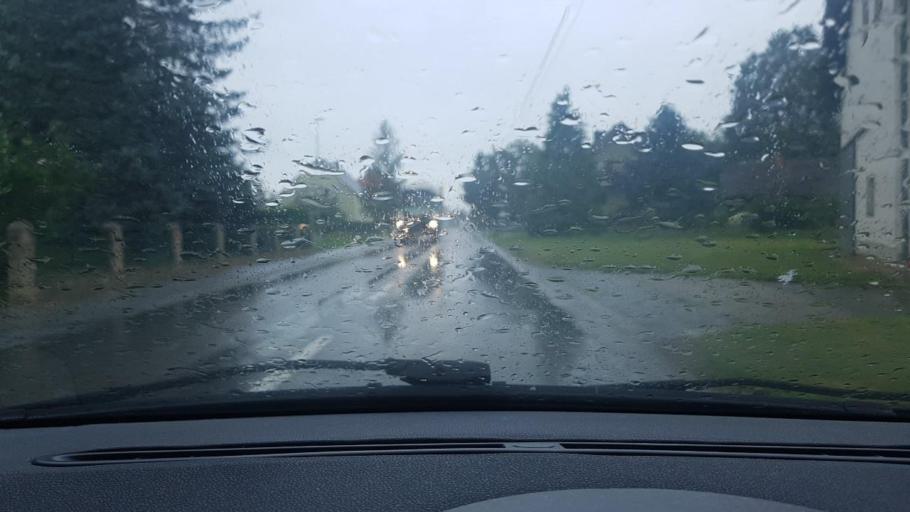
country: AT
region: Styria
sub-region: Politischer Bezirk Graz-Umgebung
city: Zettling
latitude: 46.9523
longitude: 15.4342
